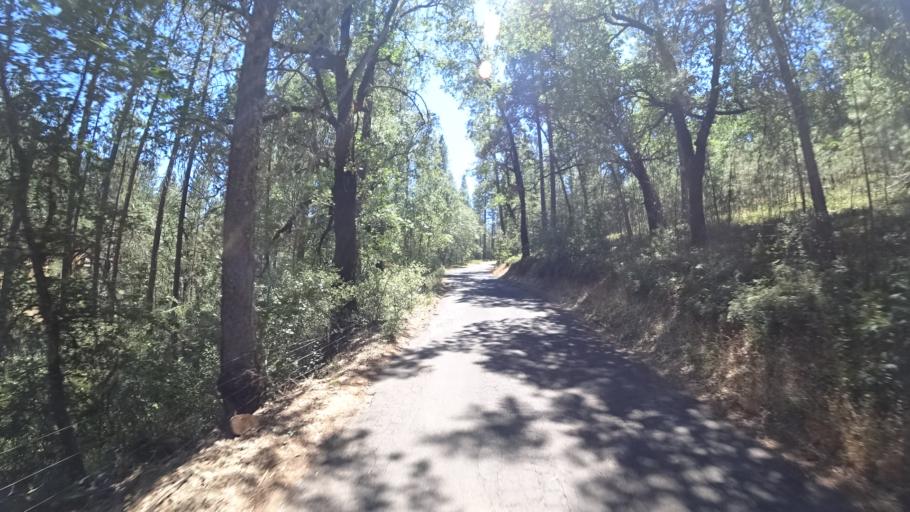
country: US
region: California
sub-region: Calaveras County
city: Mountain Ranch
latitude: 38.2672
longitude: -120.4915
